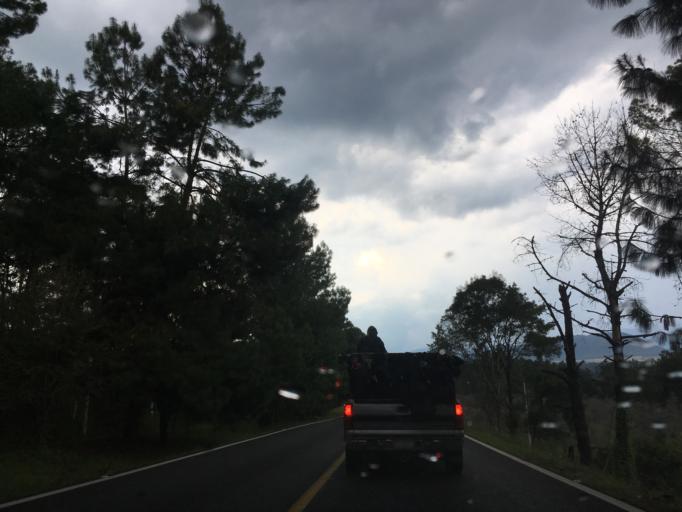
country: MX
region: Michoacan
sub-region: Patzcuaro
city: Santa Maria Huiramangaro (San Juan Tumbio)
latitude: 19.5007
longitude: -101.7558
